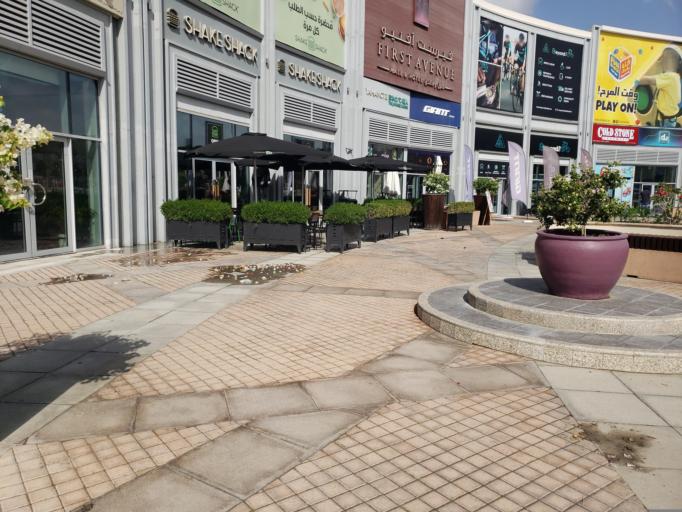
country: AE
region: Dubai
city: Dubai
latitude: 25.0471
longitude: 55.2430
